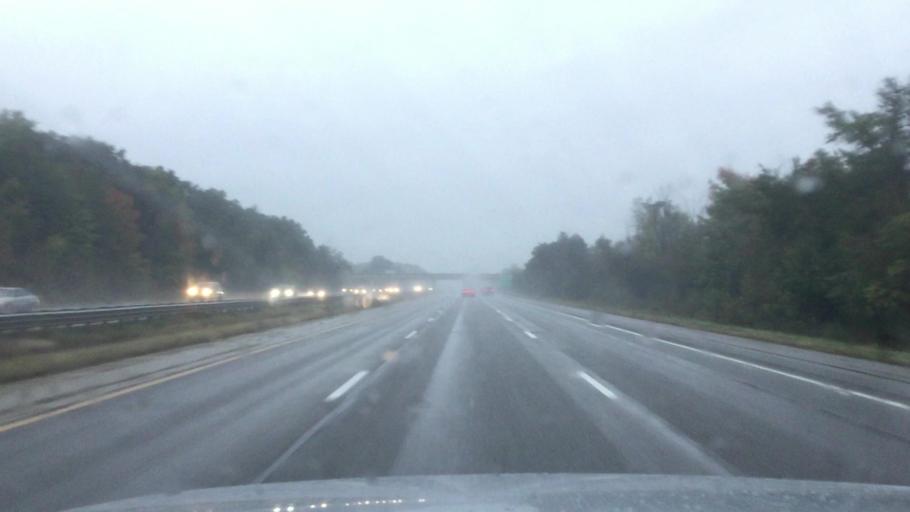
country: US
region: Michigan
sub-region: Genesee County
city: Beecher
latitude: 43.0722
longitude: -83.7625
